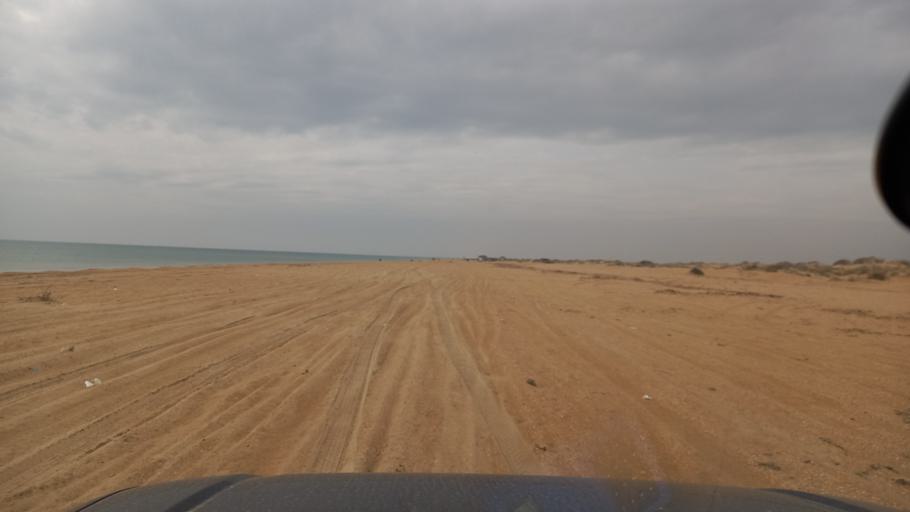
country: RU
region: Krasnodarskiy
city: Vityazevo
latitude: 44.9924
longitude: 37.2302
